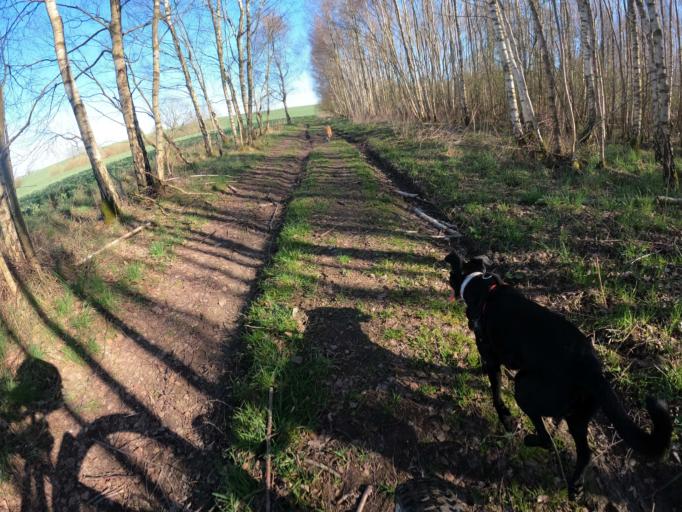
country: PL
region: West Pomeranian Voivodeship
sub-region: Powiat kolobrzeski
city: Ryman
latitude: 54.0122
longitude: 15.4791
